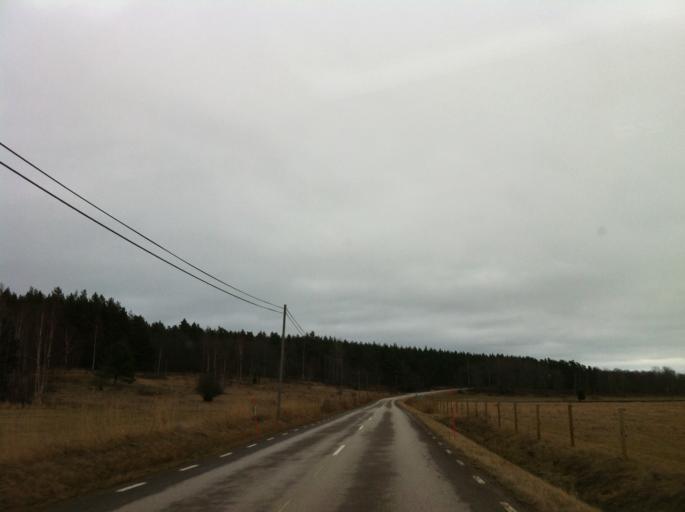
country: SE
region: Kalmar
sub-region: Vasterviks Kommun
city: Vaestervik
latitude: 57.8111
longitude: 16.5853
